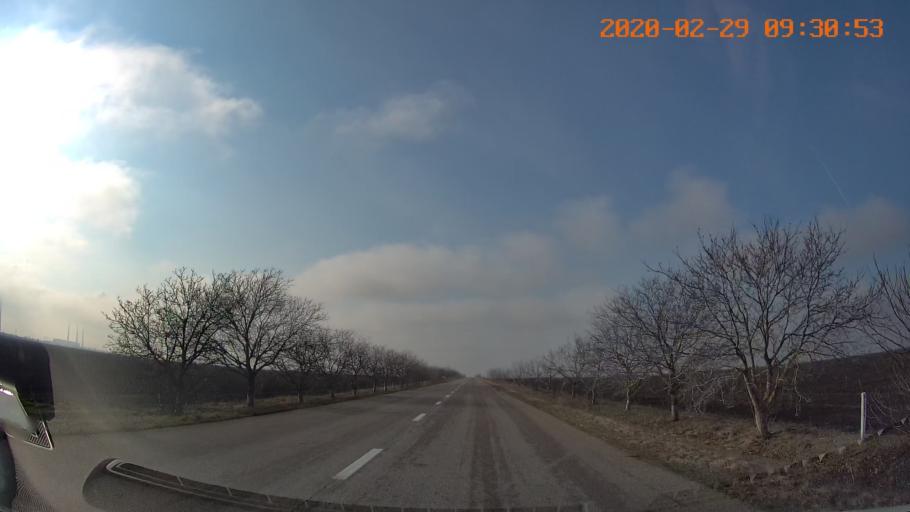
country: MD
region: Telenesti
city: Dnestrovsc
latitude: 46.6605
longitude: 29.9143
